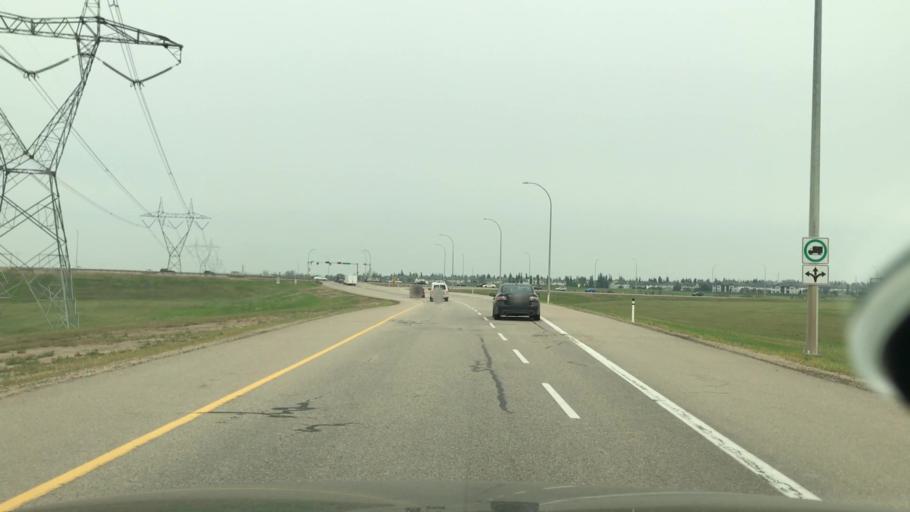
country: CA
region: Alberta
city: Devon
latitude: 53.4424
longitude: -113.5970
